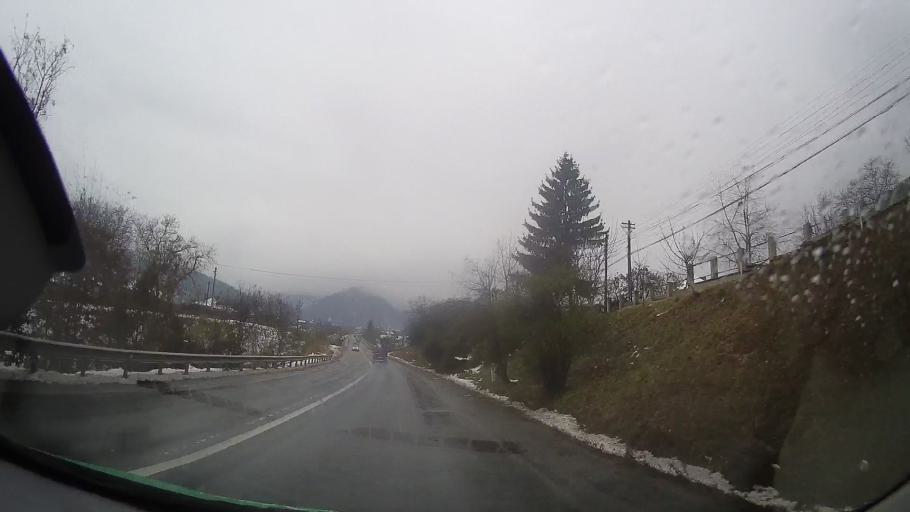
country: RO
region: Neamt
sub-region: Comuna Alexandru Cel Bun
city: Vadurele
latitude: 46.9402
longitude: 26.2666
